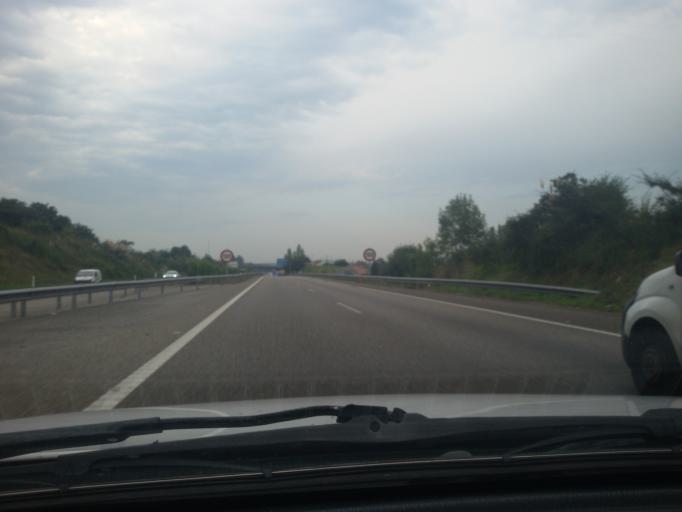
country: ES
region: Asturias
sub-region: Province of Asturias
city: Lugones
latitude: 43.3897
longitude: -5.8273
